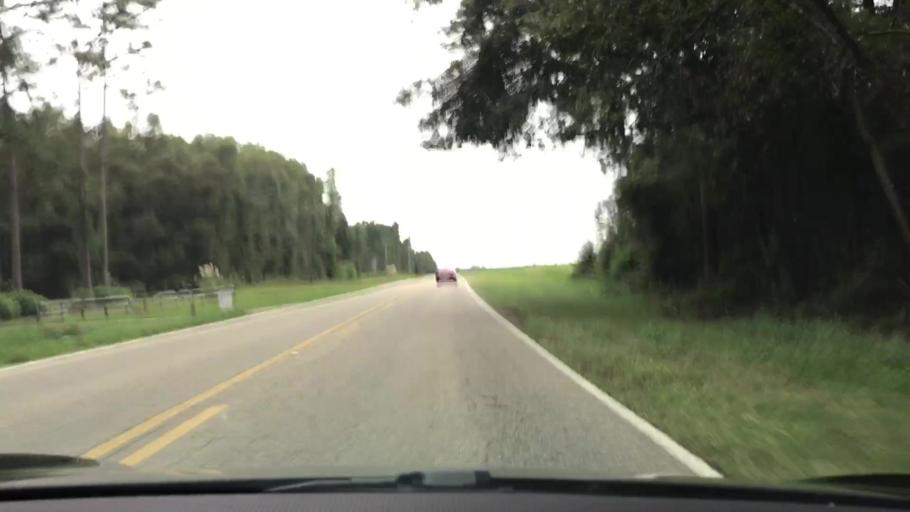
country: US
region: Alabama
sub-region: Geneva County
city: Samson
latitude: 31.1431
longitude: -86.1380
